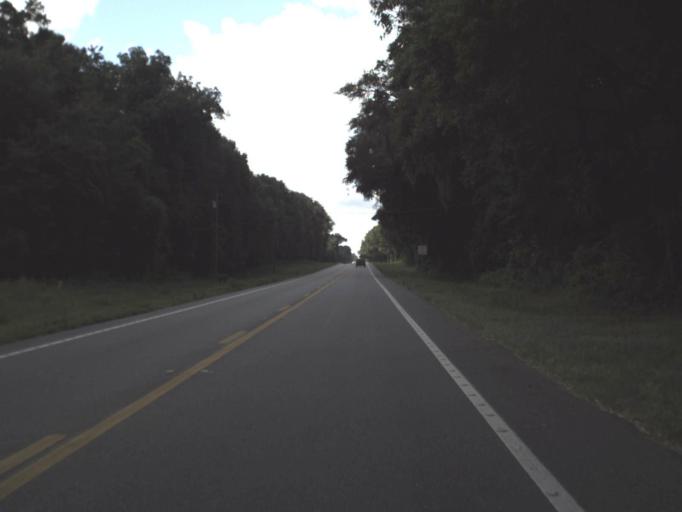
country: US
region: Florida
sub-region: Alachua County
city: High Springs
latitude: 29.9023
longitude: -82.8600
